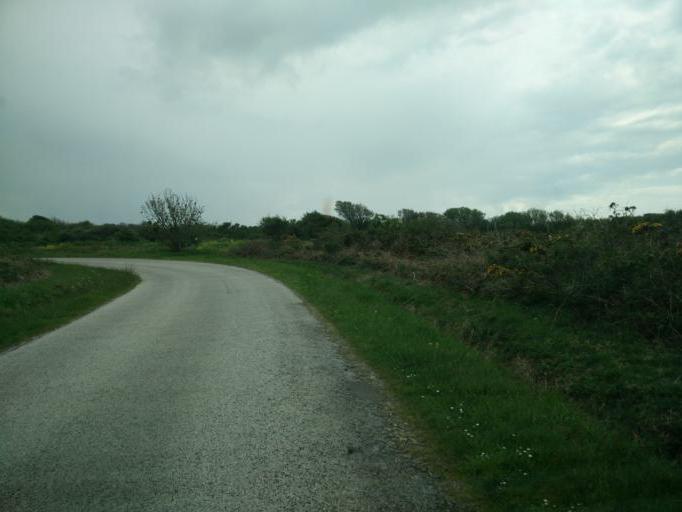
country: FR
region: Brittany
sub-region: Departement du Finistere
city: Roscanvel
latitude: 48.3014
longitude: -4.5650
